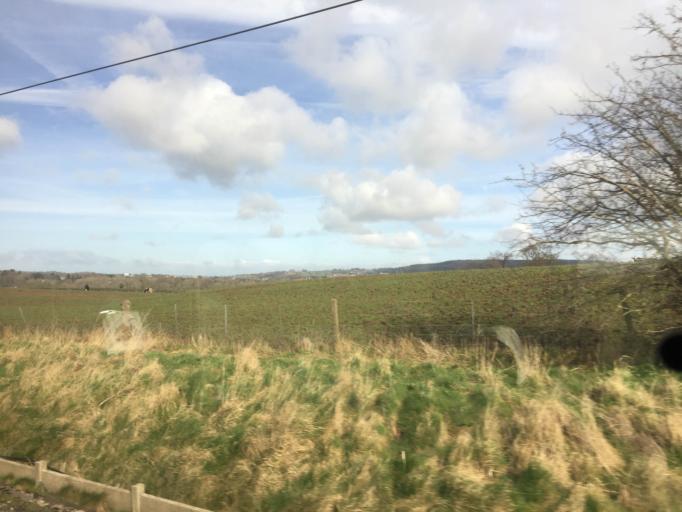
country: GB
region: England
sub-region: Cumbria
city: Penrith
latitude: 54.6382
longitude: -2.7491
